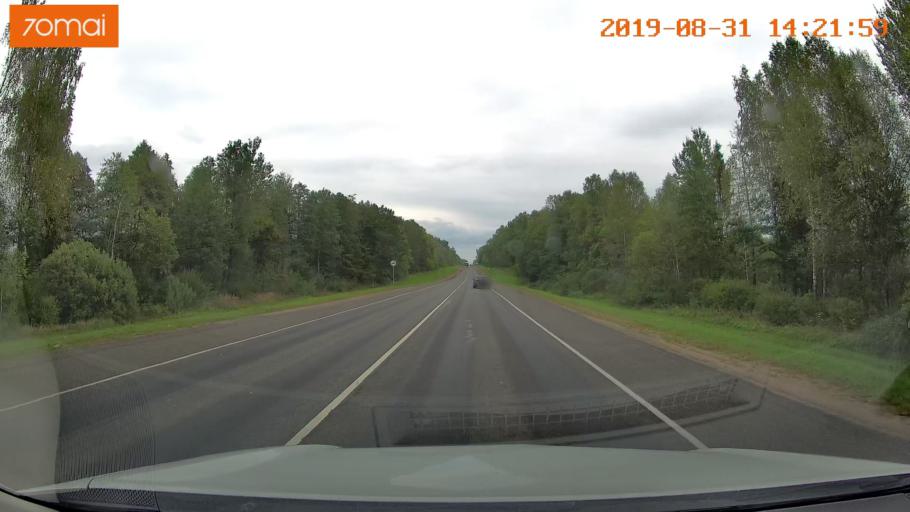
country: RU
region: Smolensk
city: Yekimovichi
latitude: 54.0887
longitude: 33.2081
